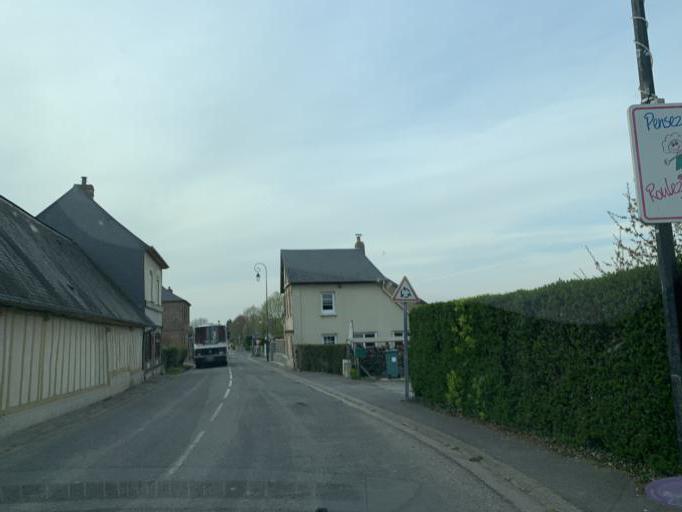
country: FR
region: Haute-Normandie
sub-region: Departement de la Seine-Maritime
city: La Mailleraye-sur-Seine
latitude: 49.4935
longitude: 0.7642
